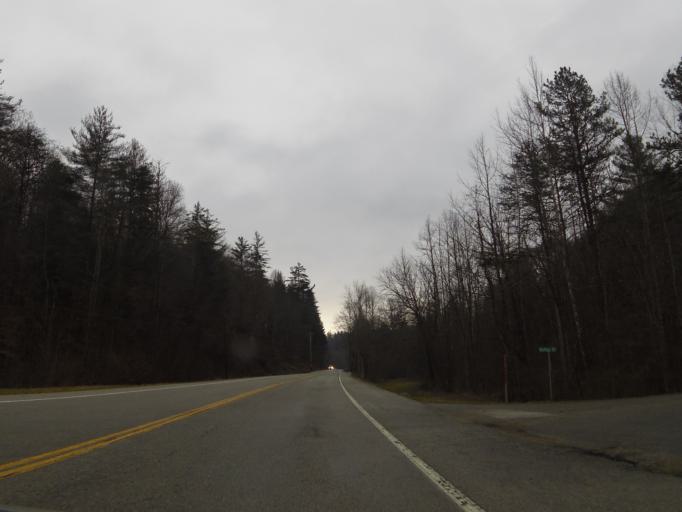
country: US
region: Tennessee
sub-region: Roane County
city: Harriman
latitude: 36.0189
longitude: -84.5267
